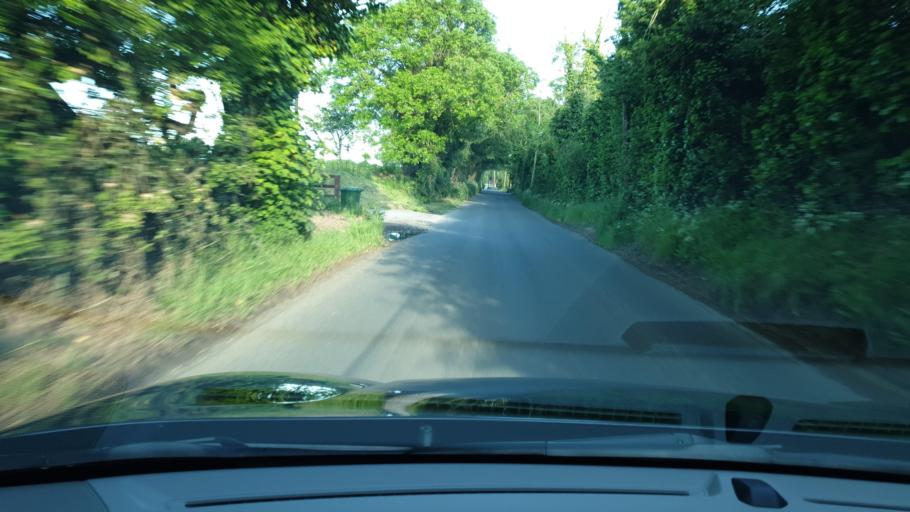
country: IE
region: Leinster
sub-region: An Mhi
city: Ashbourne
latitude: 53.5357
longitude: -6.3207
